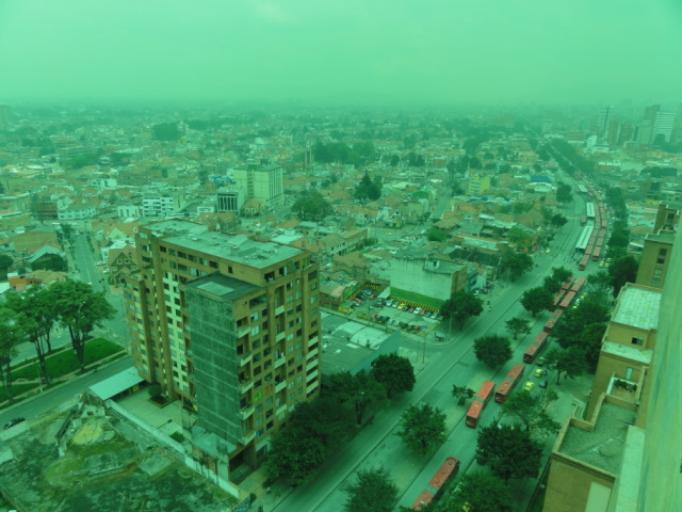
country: CO
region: Bogota D.C.
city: Bogota
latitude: 4.6183
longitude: -74.0709
